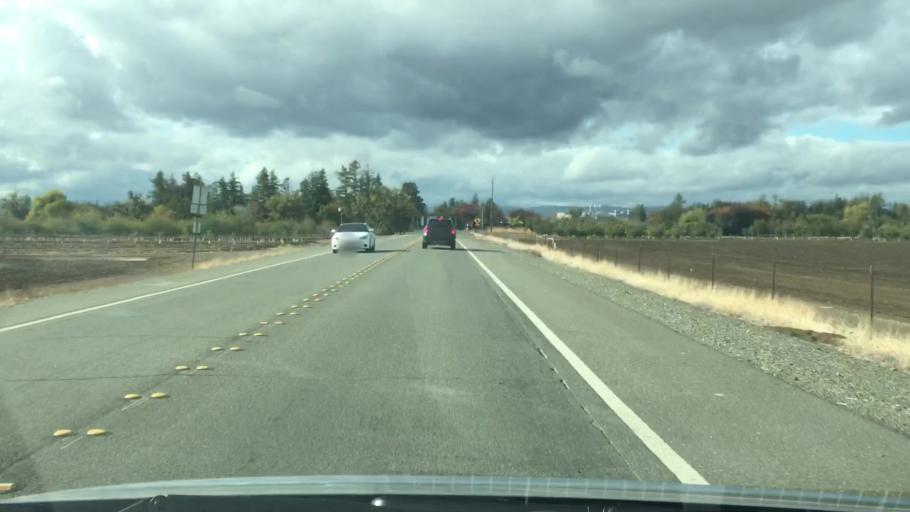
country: US
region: California
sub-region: Yolo County
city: Davis
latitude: 38.5398
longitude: -121.8005
